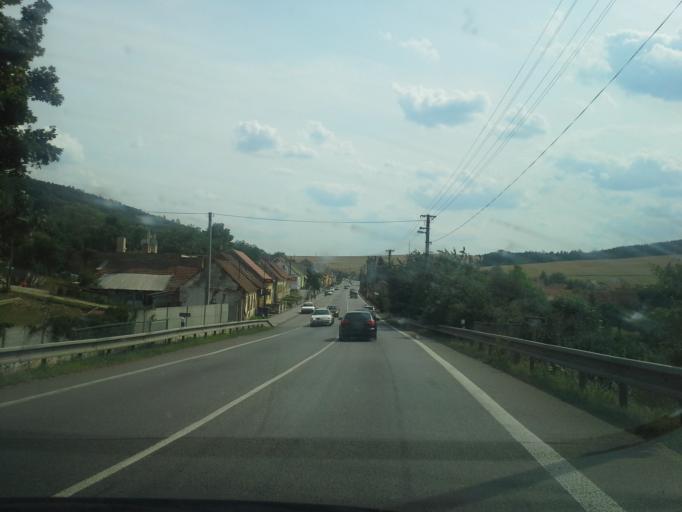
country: CZ
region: South Moravian
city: Lipuvka
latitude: 49.3569
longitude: 16.5520
